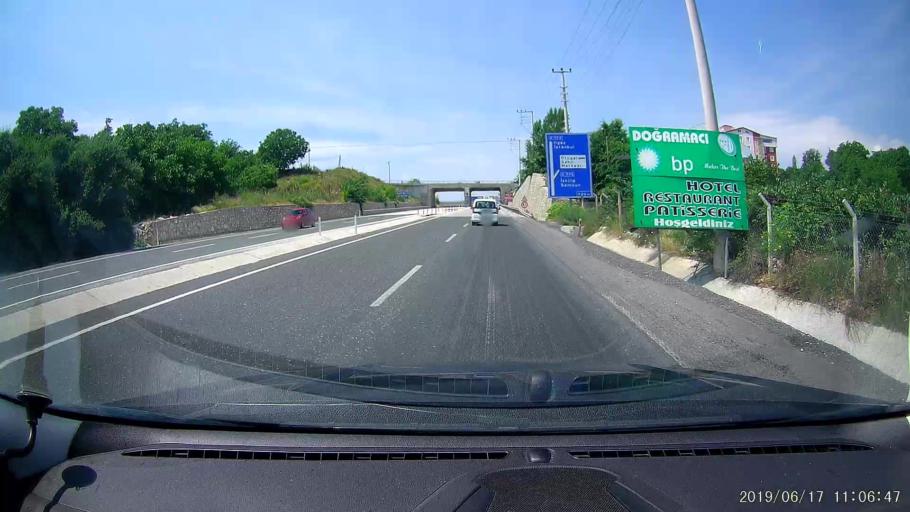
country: TR
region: Kastamonu
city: Tosya
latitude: 41.0098
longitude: 34.0621
